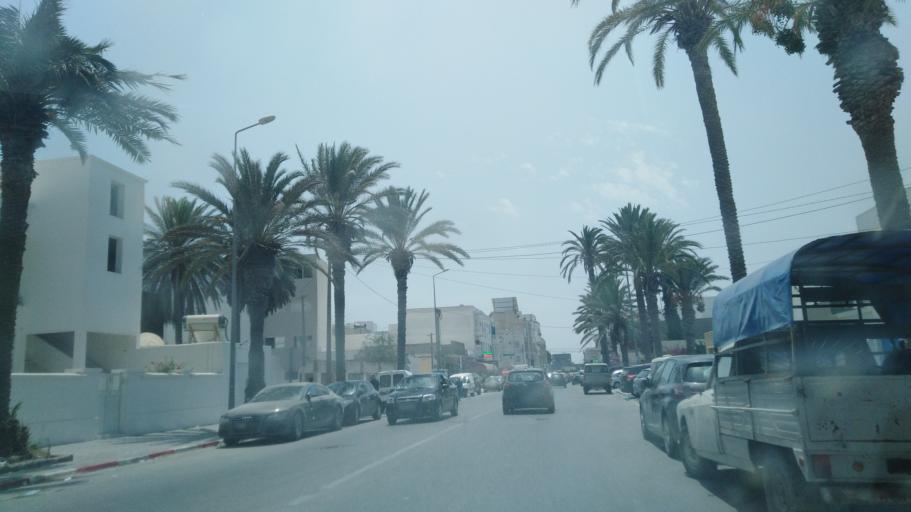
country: TN
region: Al Mahdiyah
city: Mahdia
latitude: 35.5108
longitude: 11.0524
